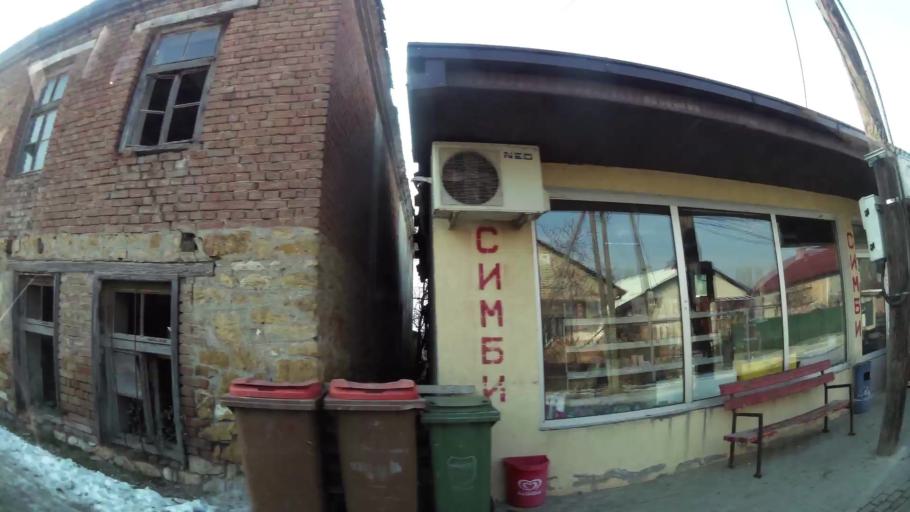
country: MK
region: Suto Orizari
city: Suto Orizare
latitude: 42.0276
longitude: 21.3743
